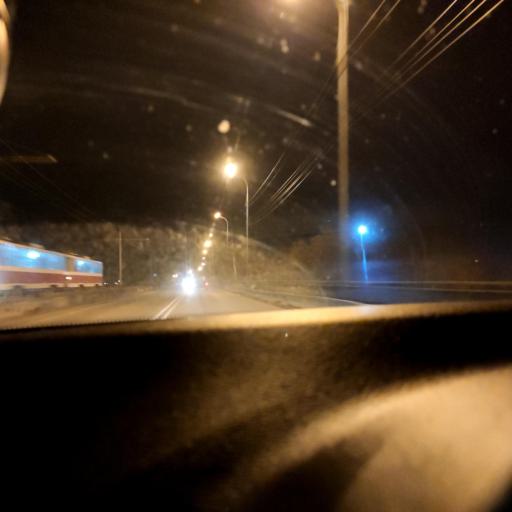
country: RU
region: Samara
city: Smyshlyayevka
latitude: 53.2194
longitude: 50.2902
